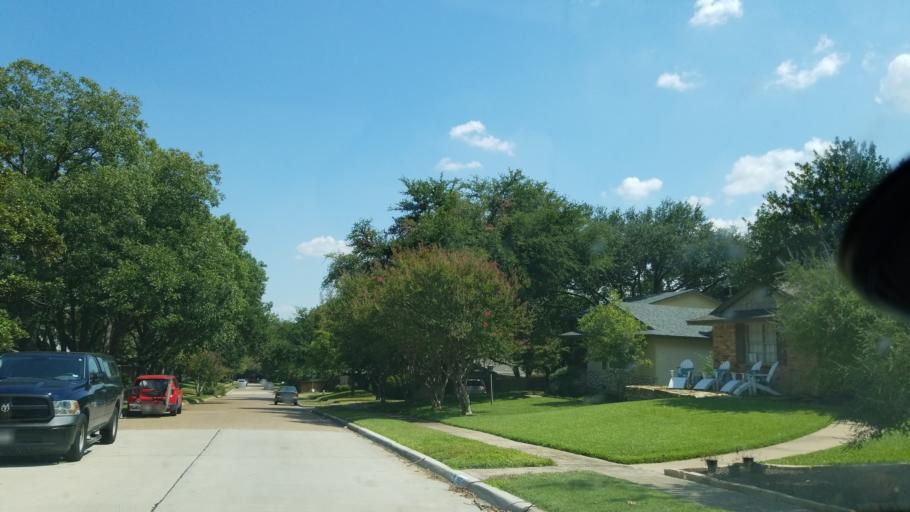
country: US
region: Texas
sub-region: Dallas County
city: Richardson
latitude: 32.8836
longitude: -96.7160
